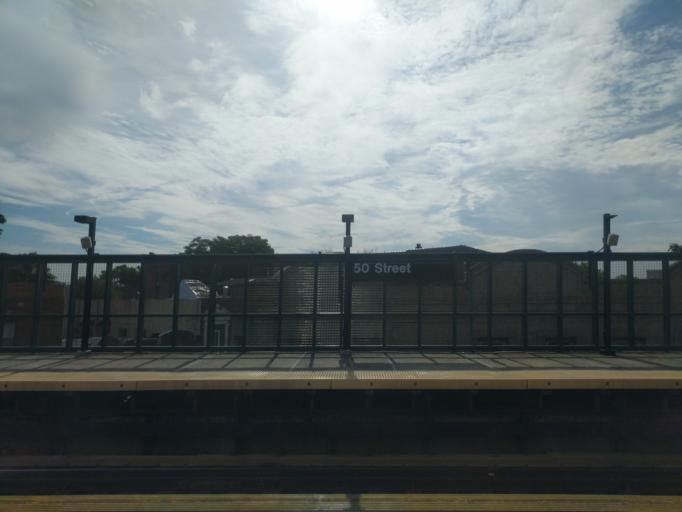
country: US
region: New York
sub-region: Kings County
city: Bensonhurst
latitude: 40.6356
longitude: -73.9949
